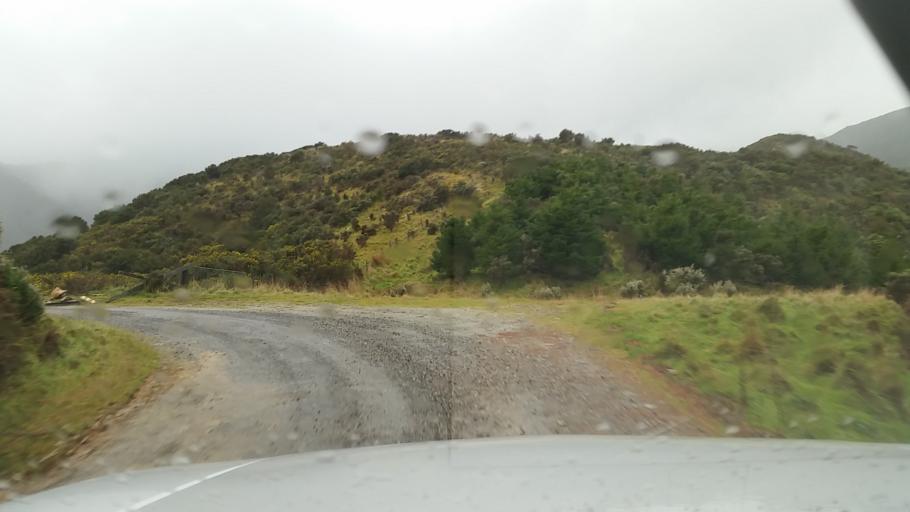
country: NZ
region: Marlborough
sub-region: Marlborough District
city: Picton
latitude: -41.1364
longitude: 174.0577
